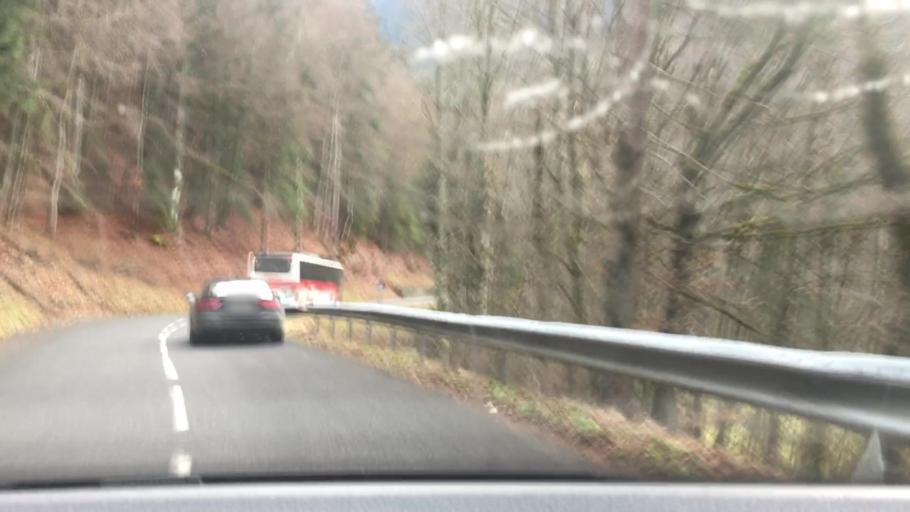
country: FR
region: Rhone-Alpes
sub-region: Departement de la Haute-Savoie
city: Abondance
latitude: 46.2546
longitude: 6.6305
